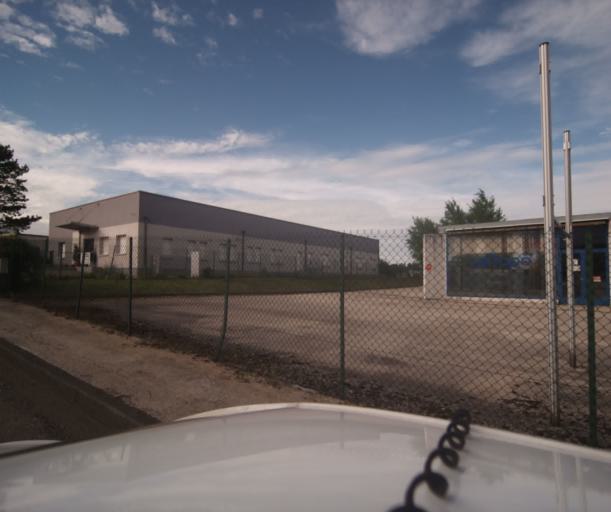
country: FR
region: Franche-Comte
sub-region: Departement du Doubs
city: Pirey
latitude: 47.2362
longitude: 5.9817
